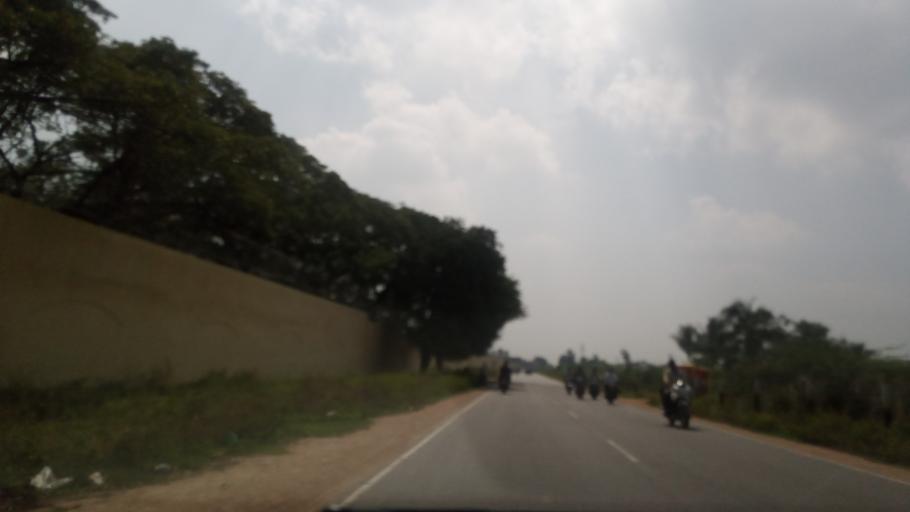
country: IN
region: Tamil Nadu
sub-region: Vellore
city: Arakkonam
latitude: 13.0629
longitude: 79.6737
